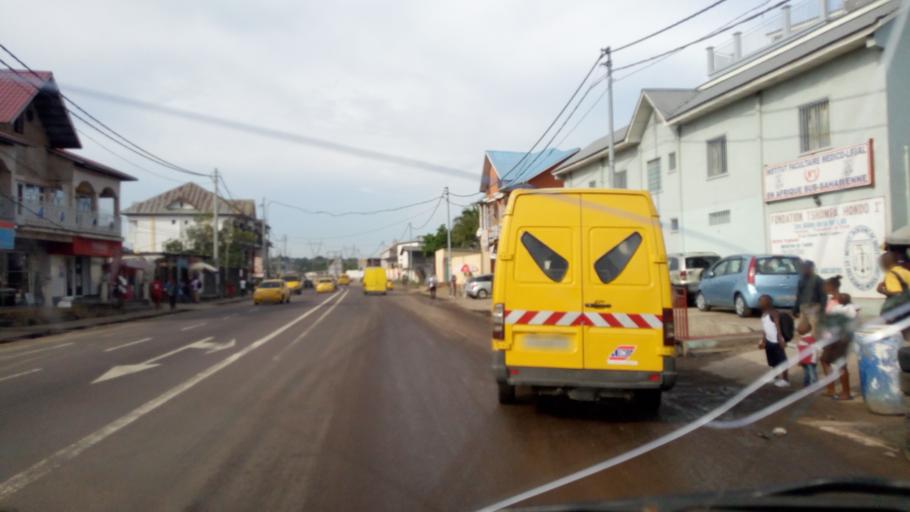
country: CD
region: Kinshasa
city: Kinshasa
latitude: -4.4385
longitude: 15.2573
